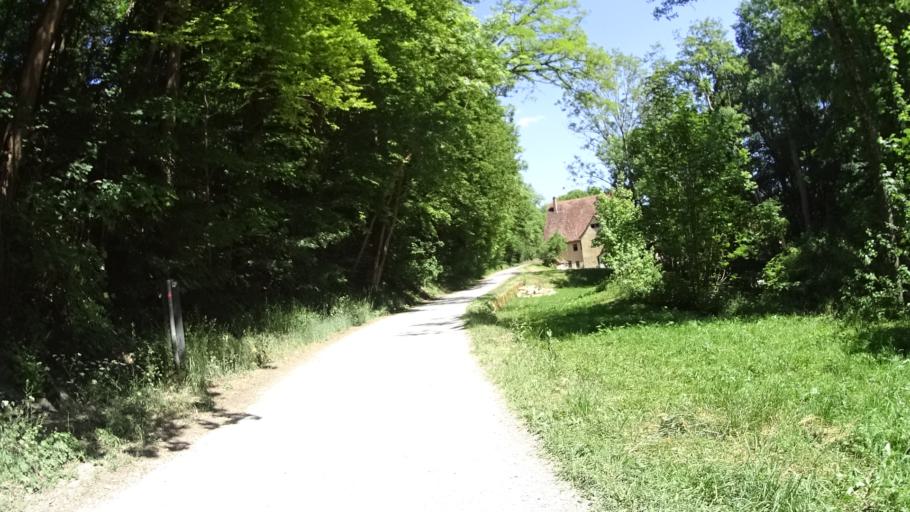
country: DE
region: Bavaria
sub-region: Regierungsbezirk Mittelfranken
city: Rothenburg ob der Tauber
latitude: 49.3628
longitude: 10.1894
